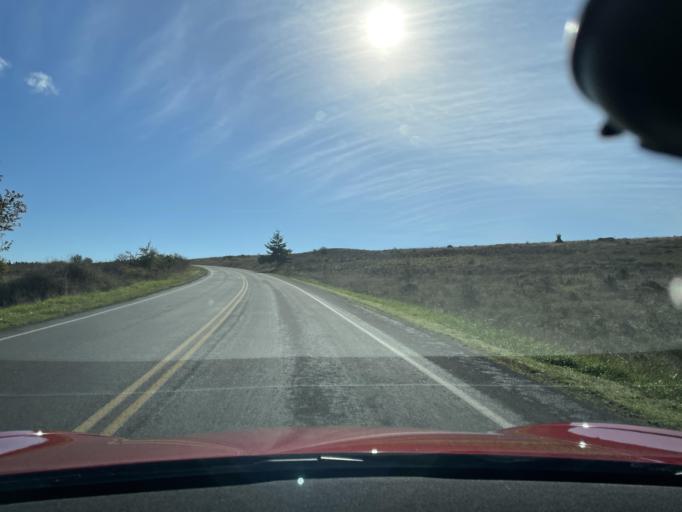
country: US
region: Washington
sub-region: San Juan County
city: Friday Harbor
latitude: 48.4658
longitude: -123.0060
